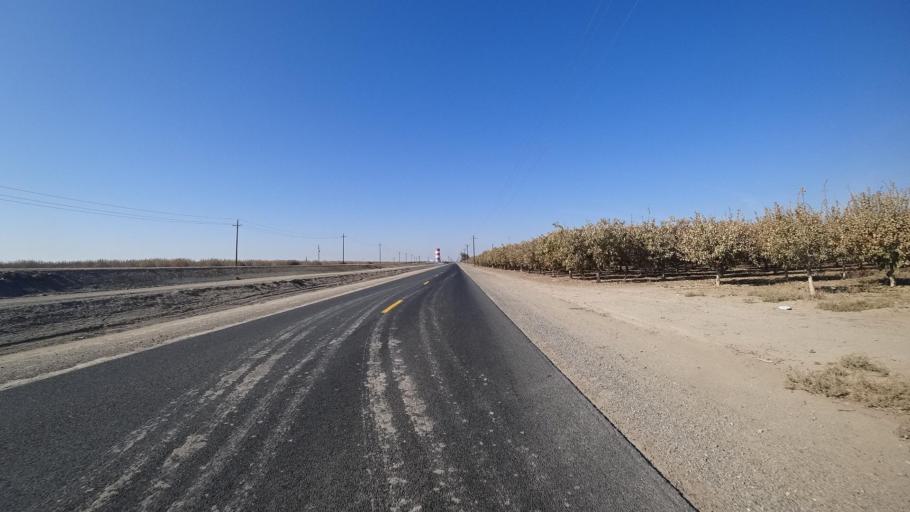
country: US
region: California
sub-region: Kern County
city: Wasco
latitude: 35.7176
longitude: -119.3952
